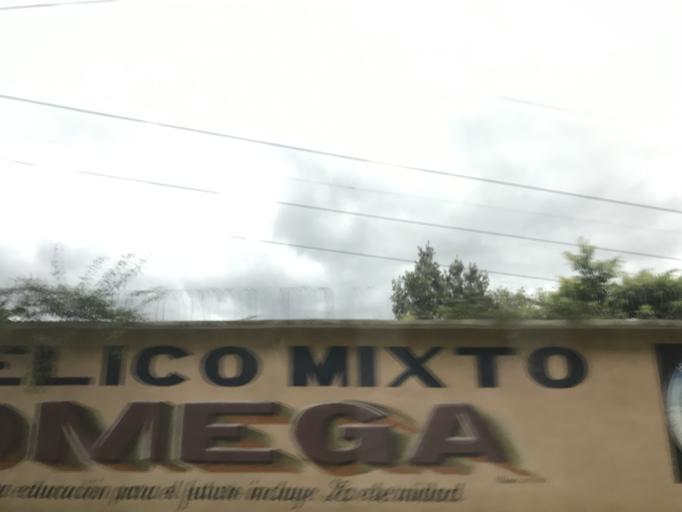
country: GT
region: Chimaltenango
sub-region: Municipio de Chimaltenango
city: Chimaltenango
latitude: 14.6701
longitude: -90.8509
